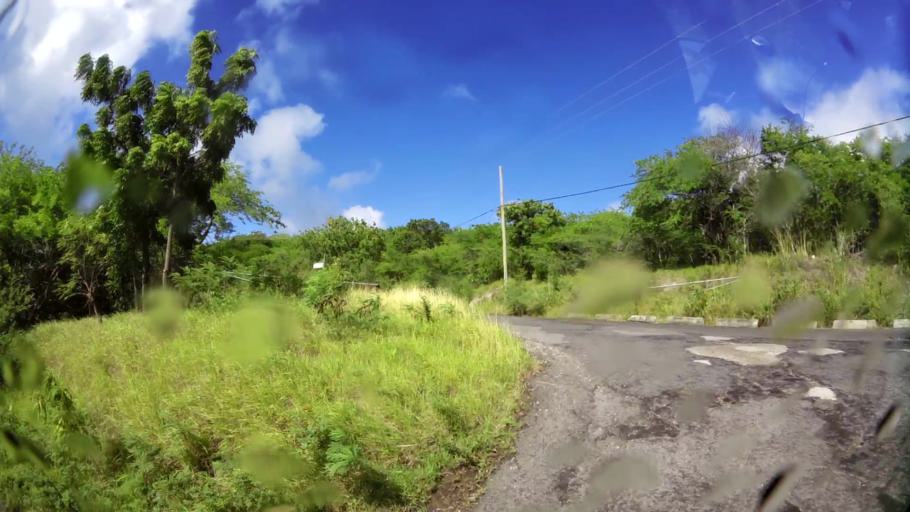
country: MS
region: Saint Peter
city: Saint Peters
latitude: 16.7452
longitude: -62.2286
